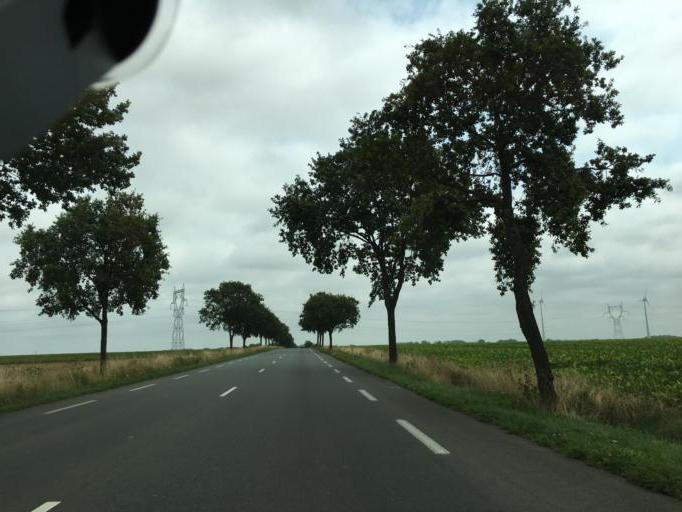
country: FR
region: Nord-Pas-de-Calais
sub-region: Departement du Pas-de-Calais
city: Saint-Pol-sur-Ternoise
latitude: 50.4137
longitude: 2.3865
